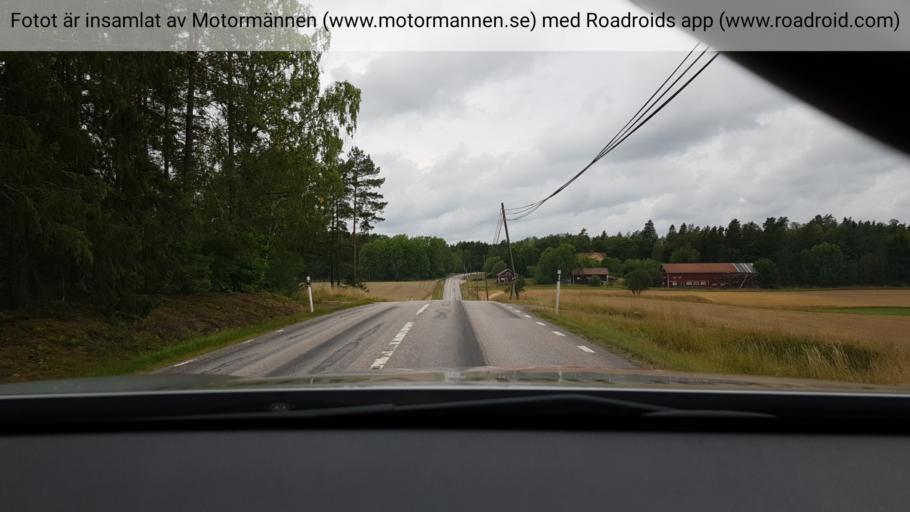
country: SE
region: Soedermanland
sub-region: Strangnas Kommun
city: Akers Styckebruk
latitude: 59.0724
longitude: 17.1223
